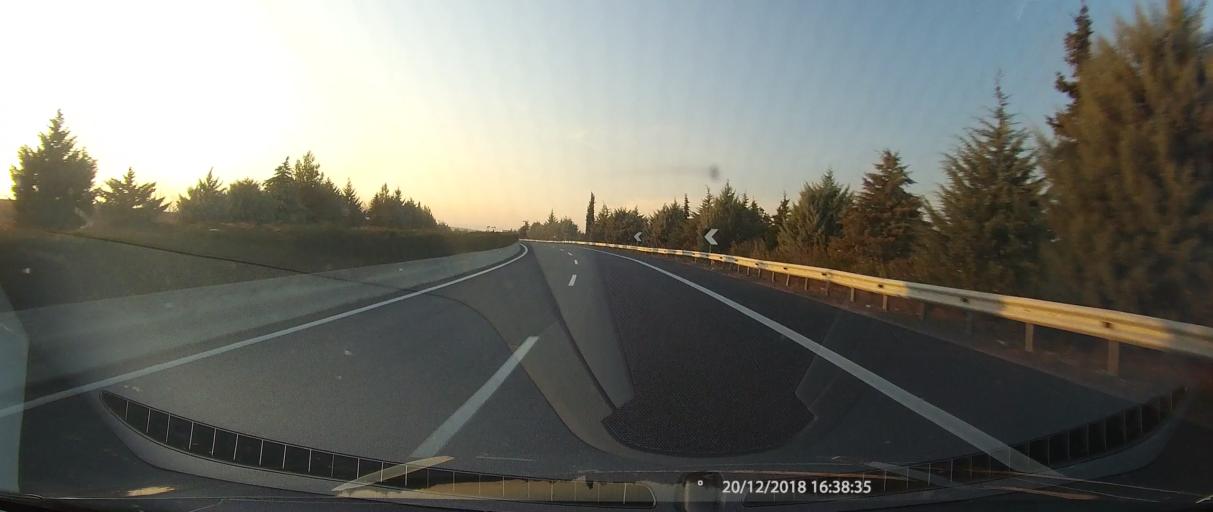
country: GR
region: Thessaly
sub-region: Nomos Magnisias
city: Velestino
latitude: 39.3462
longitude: 22.7809
